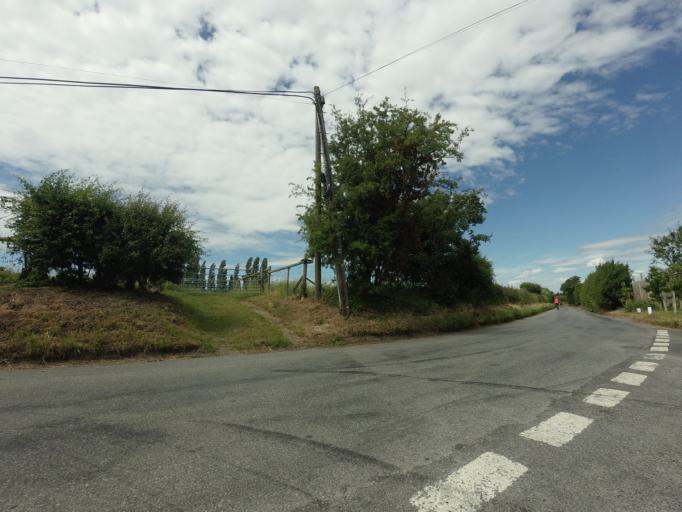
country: GB
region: England
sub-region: Kent
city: Strood
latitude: 51.4234
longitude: 0.4812
